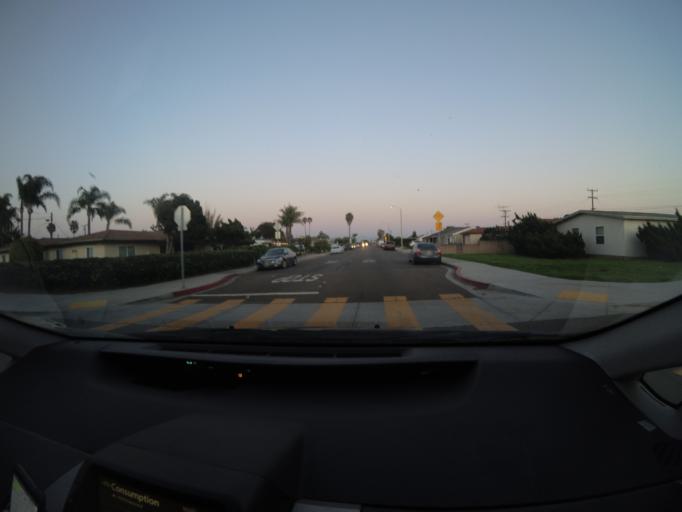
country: US
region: California
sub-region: San Diego County
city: Imperial Beach
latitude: 32.5803
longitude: -117.1276
